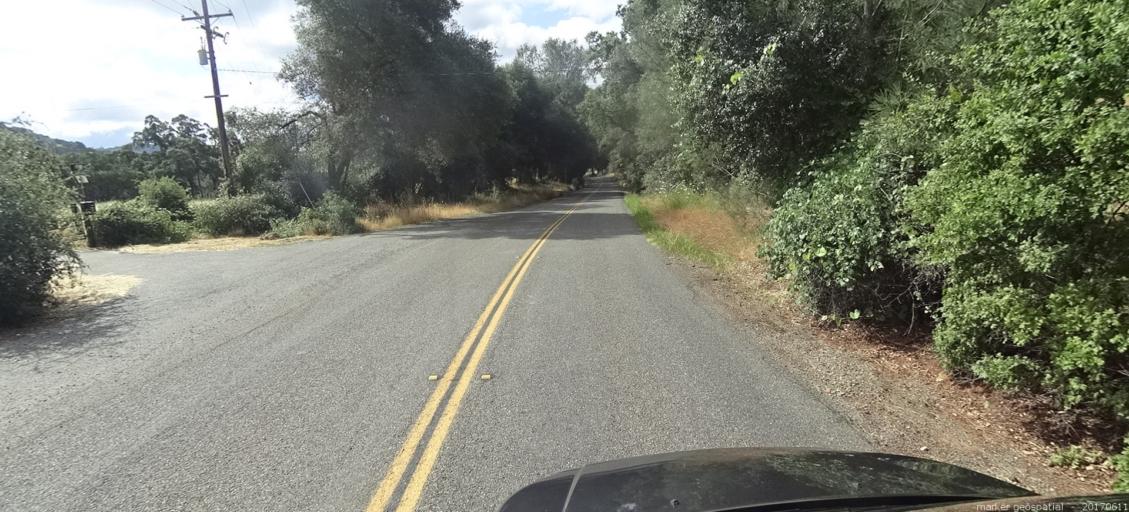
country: US
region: California
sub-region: Yuba County
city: Loma Rica
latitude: 39.3757
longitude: -121.3764
